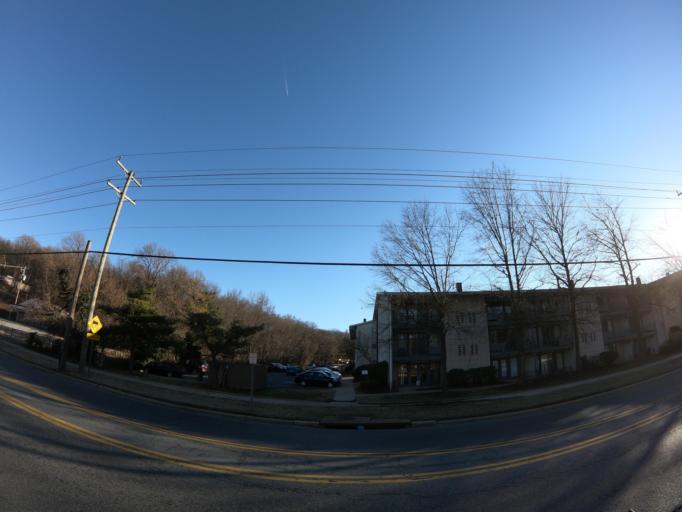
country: US
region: Maryland
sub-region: Prince George's County
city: Woodlawn
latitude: 38.9644
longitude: -76.8959
